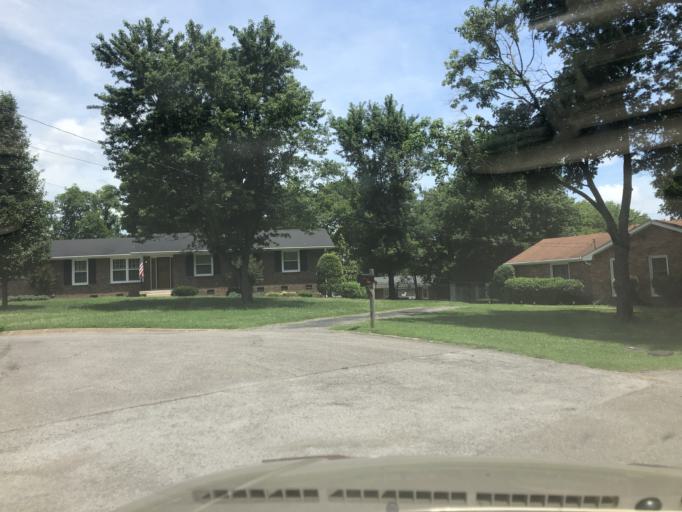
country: US
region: Tennessee
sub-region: Davidson County
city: Lakewood
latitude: 36.2486
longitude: -86.6731
